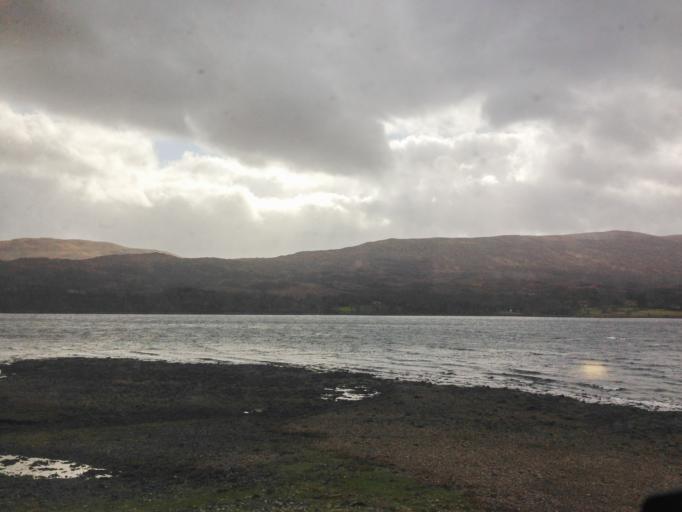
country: GB
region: Scotland
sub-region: Highland
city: Fort William
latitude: 56.8548
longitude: -5.1899
